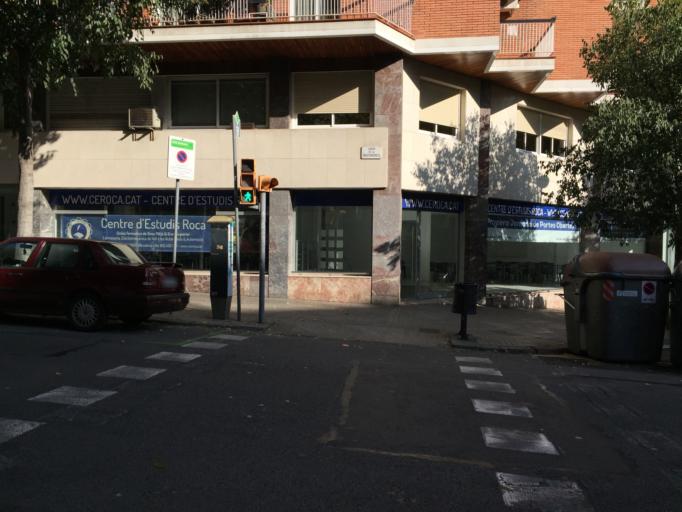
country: ES
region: Catalonia
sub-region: Provincia de Barcelona
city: Horta-Guinardo
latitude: 41.4121
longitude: 2.1777
